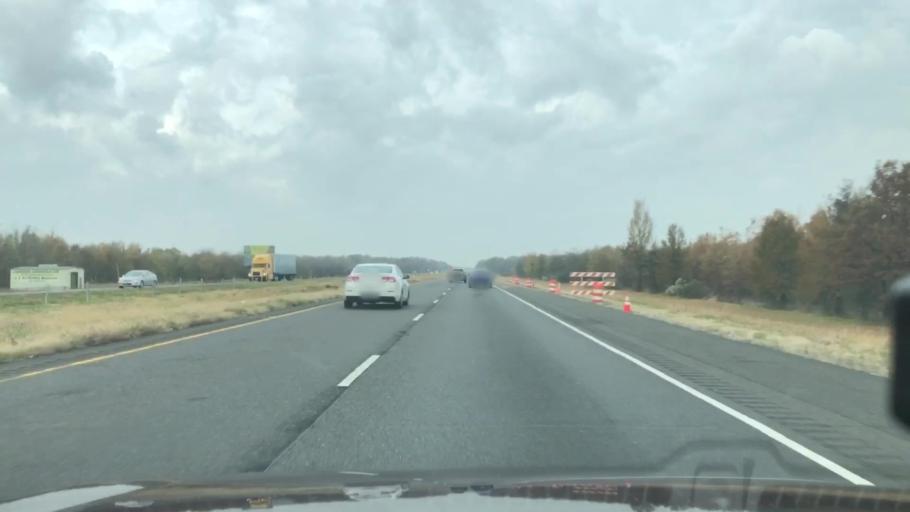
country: US
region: Louisiana
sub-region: Richland Parish
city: Delhi
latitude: 32.4380
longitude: -91.4618
